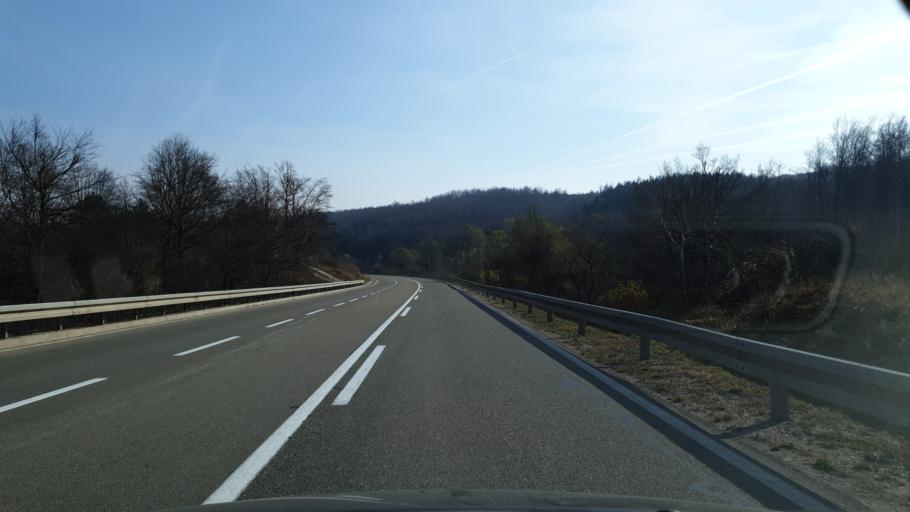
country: RS
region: Central Serbia
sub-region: Nisavski Okrug
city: Razanj
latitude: 43.8426
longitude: 21.6827
